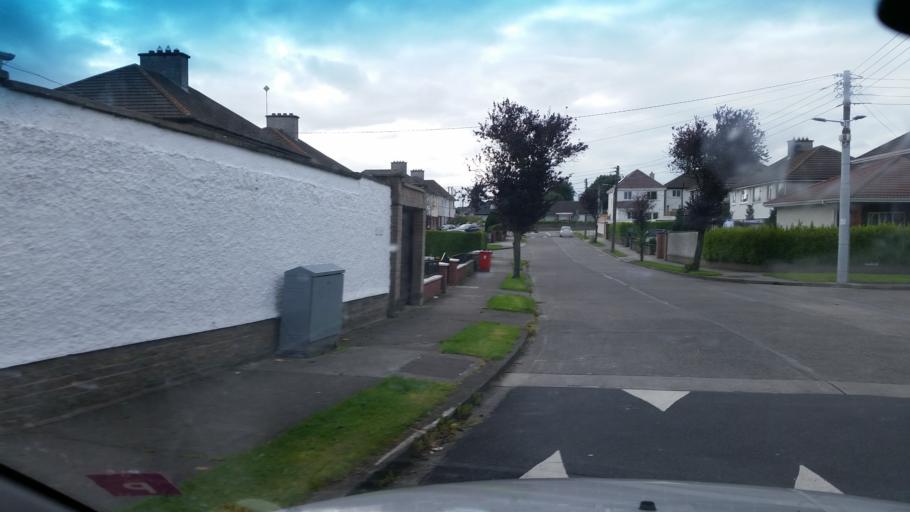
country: IE
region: Leinster
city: Ballymun
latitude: 53.3878
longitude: -6.2776
